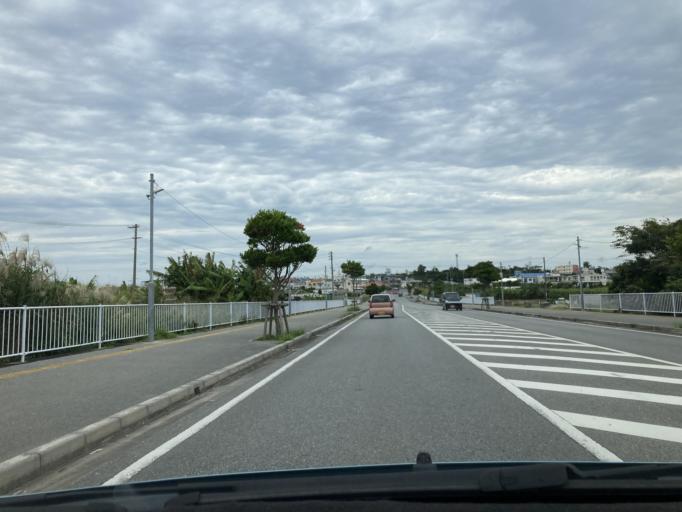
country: JP
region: Okinawa
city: Ishikawa
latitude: 26.3991
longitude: 127.7400
